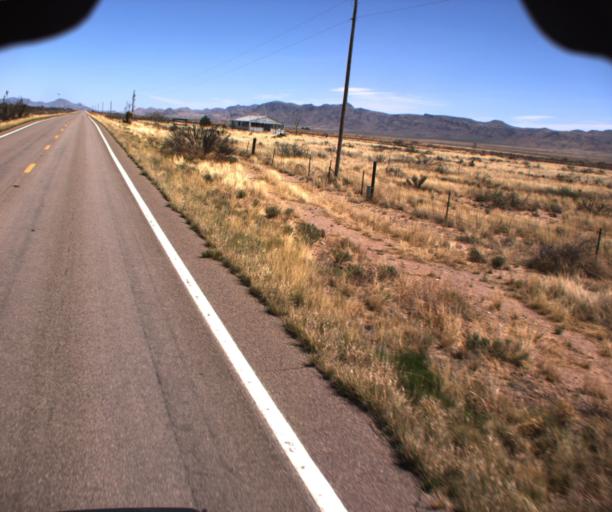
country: US
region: Arizona
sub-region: Cochise County
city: Douglas
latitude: 31.7474
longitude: -109.0933
